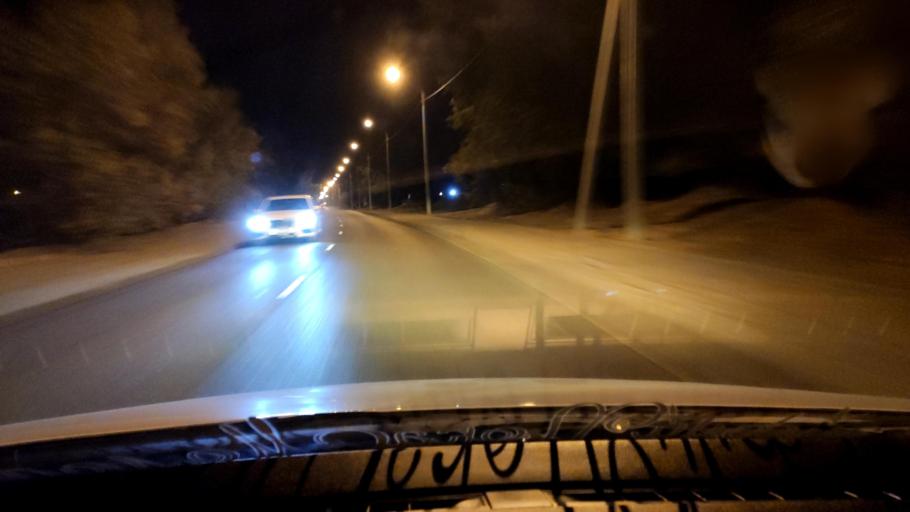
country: RU
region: Voronezj
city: Pridonskoy
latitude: 51.6909
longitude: 39.0824
